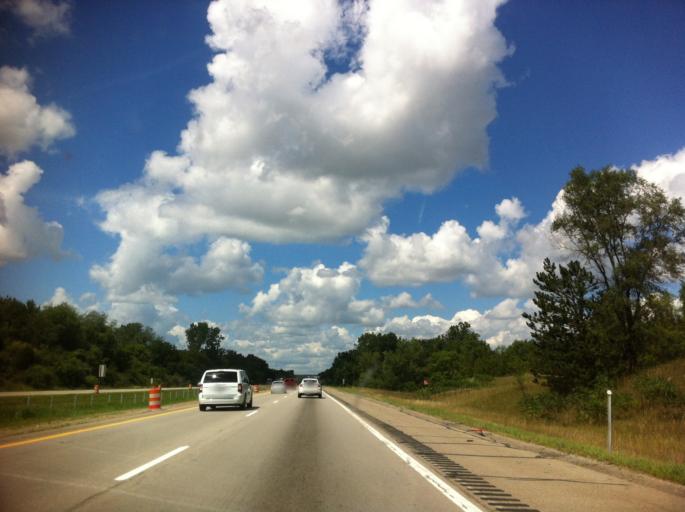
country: US
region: Michigan
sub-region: Washtenaw County
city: Milan
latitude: 42.1451
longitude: -83.6835
